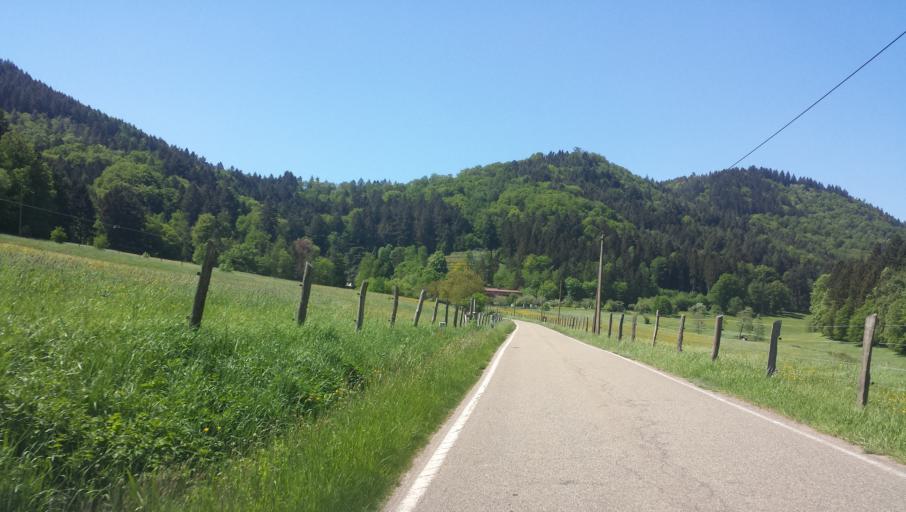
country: DE
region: Rheinland-Pfalz
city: Ramberg
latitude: 49.2705
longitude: 8.0372
